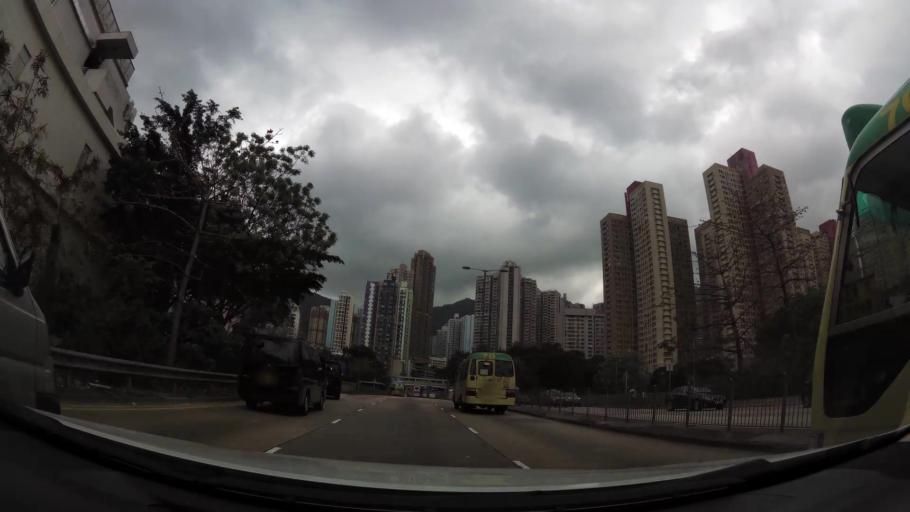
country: HK
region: Wong Tai Sin
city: Wong Tai Sin
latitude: 22.3411
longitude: 114.1983
